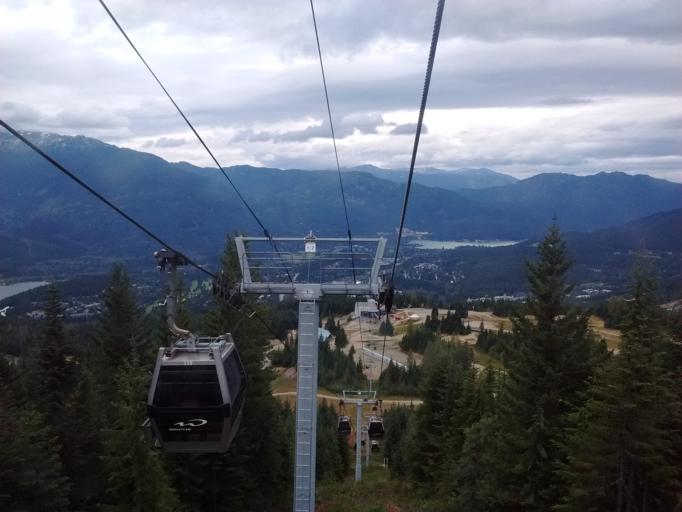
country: CA
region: British Columbia
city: Whistler
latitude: 50.0937
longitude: -122.9506
